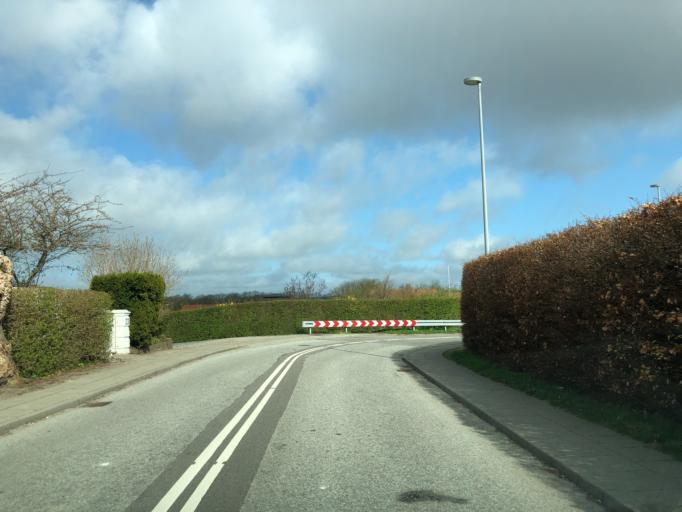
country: DK
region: North Denmark
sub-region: Alborg Kommune
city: Aalborg
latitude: 57.0491
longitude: 9.8942
